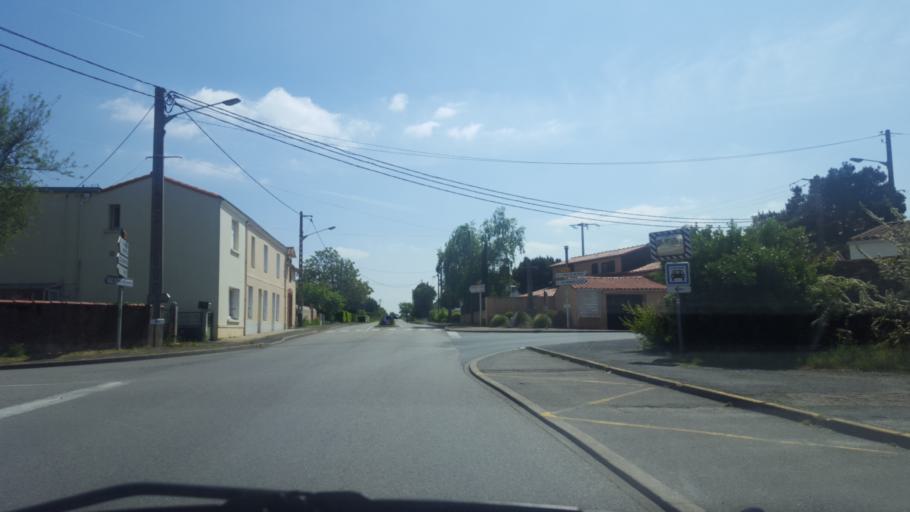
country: FR
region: Pays de la Loire
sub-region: Departement de la Loire-Atlantique
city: La Limouziniere
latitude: 47.0142
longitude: -1.5702
